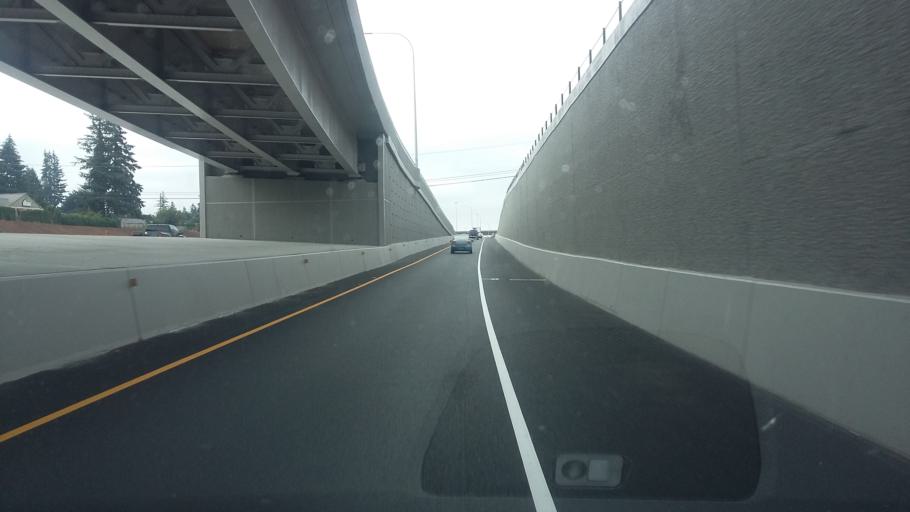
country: US
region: Washington
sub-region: Clark County
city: Orchards
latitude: 45.6331
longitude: -122.5606
